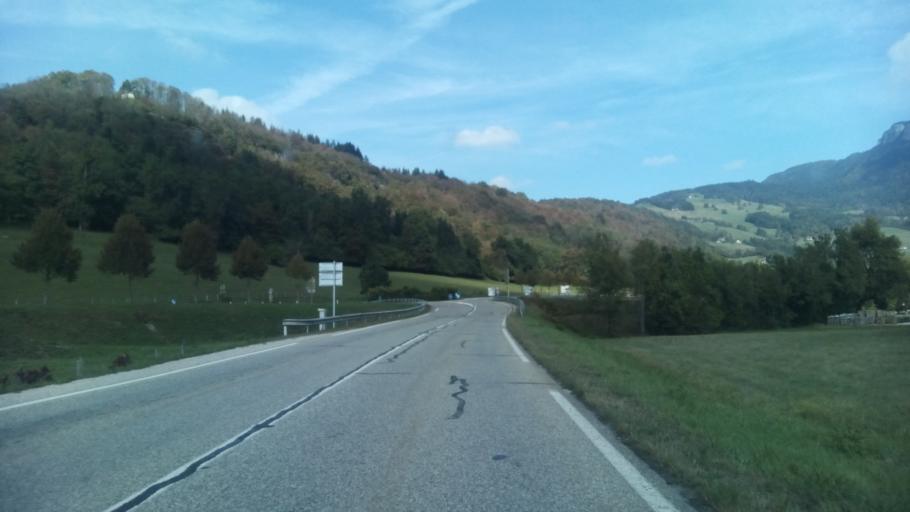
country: FR
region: Rhone-Alpes
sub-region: Departement de la Savoie
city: Les Echelles
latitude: 45.4446
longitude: 5.7638
